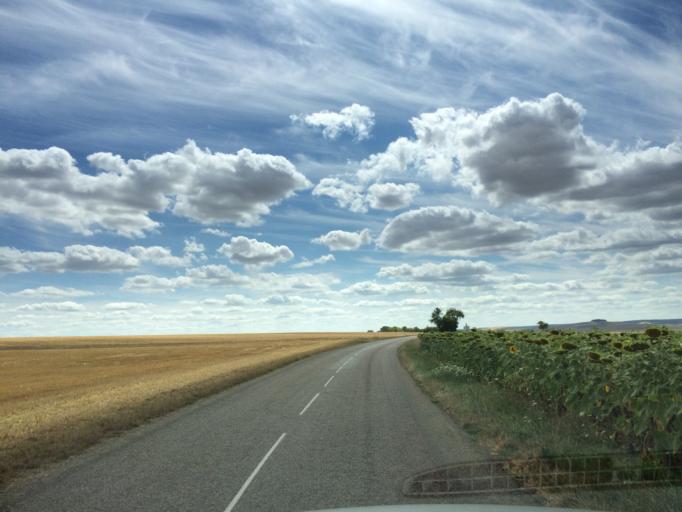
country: FR
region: Bourgogne
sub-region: Departement de l'Yonne
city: Laroche-Saint-Cydroine
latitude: 47.9327
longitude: 3.4586
